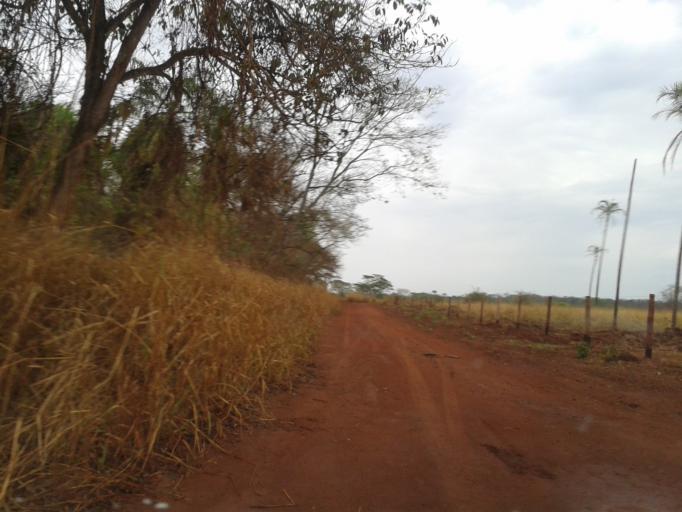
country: BR
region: Minas Gerais
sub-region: Capinopolis
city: Capinopolis
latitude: -18.8762
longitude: -49.7934
